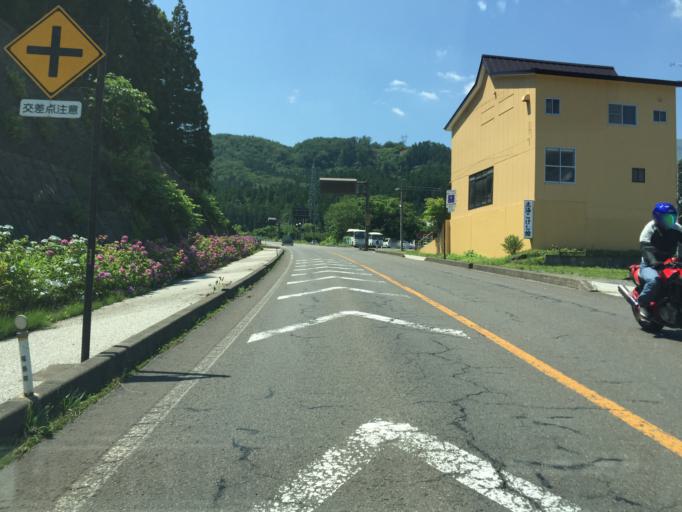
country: JP
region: Fukushima
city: Nihommatsu
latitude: 37.6831
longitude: 140.3309
